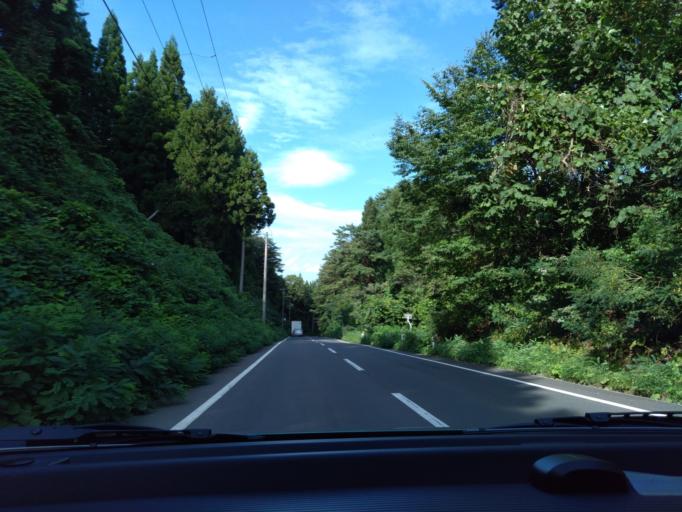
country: JP
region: Iwate
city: Morioka-shi
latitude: 39.6334
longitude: 141.0809
